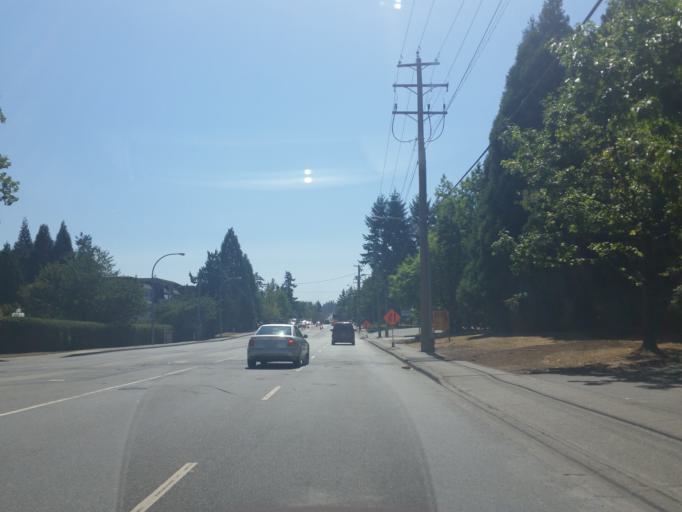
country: CA
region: British Columbia
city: Langley
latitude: 49.1069
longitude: -122.6689
